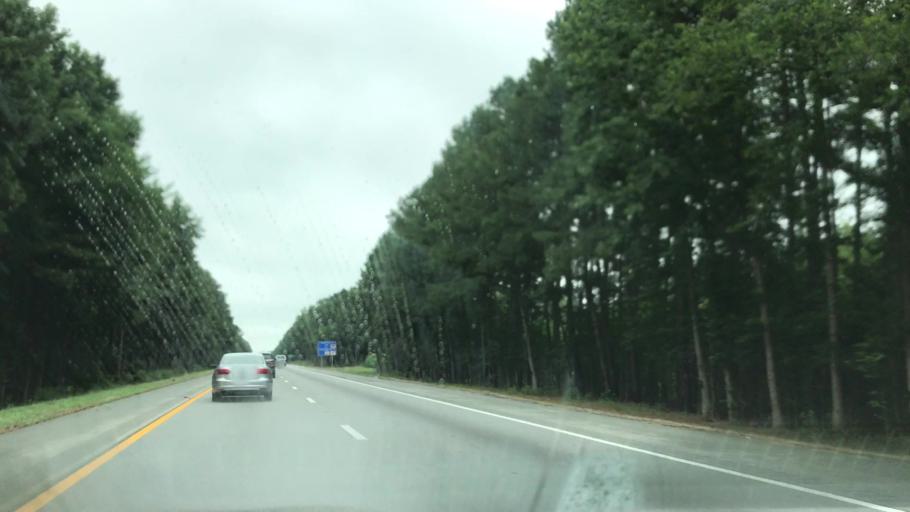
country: US
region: North Carolina
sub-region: Halifax County
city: South Rosemary
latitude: 36.3757
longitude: -77.6632
